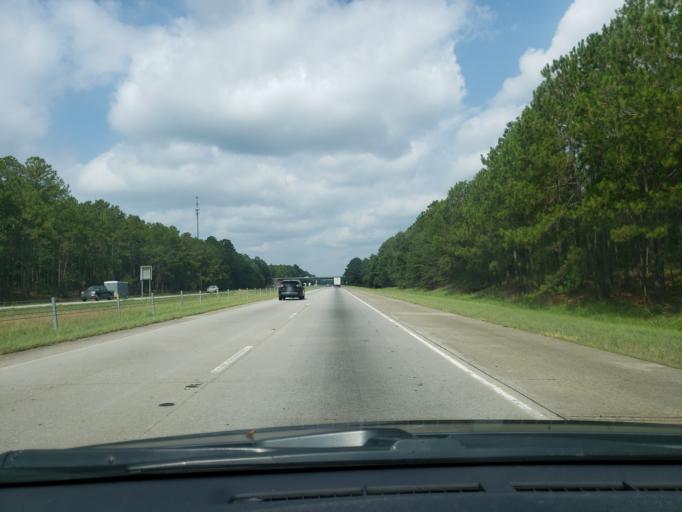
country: US
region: Georgia
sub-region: Treutlen County
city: Soperton
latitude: 32.4261
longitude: -82.4593
